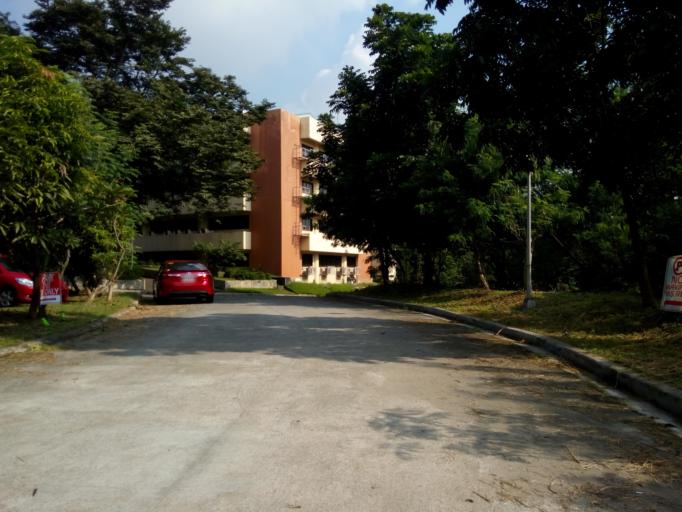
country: PH
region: Metro Manila
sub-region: Quezon City
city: Quezon City
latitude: 14.6479
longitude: 121.0687
